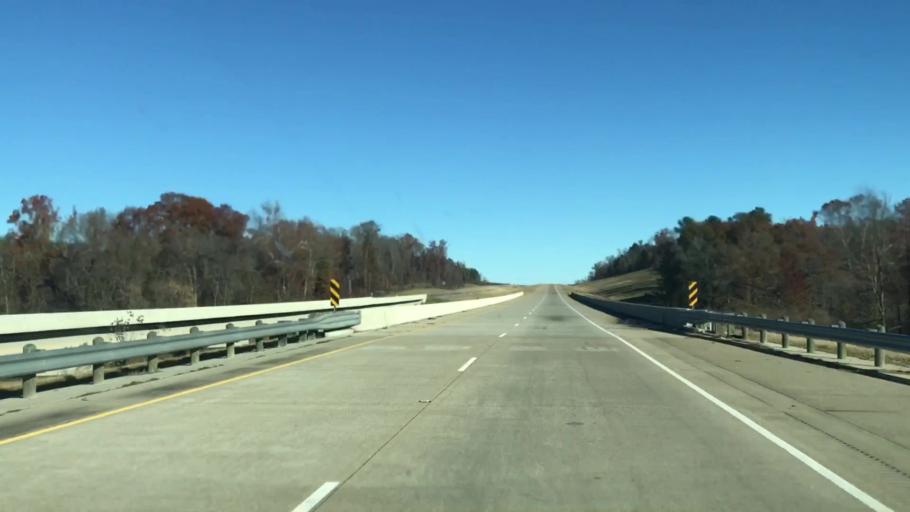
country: US
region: Louisiana
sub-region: Caddo Parish
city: Oil City
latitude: 32.7870
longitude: -93.8882
